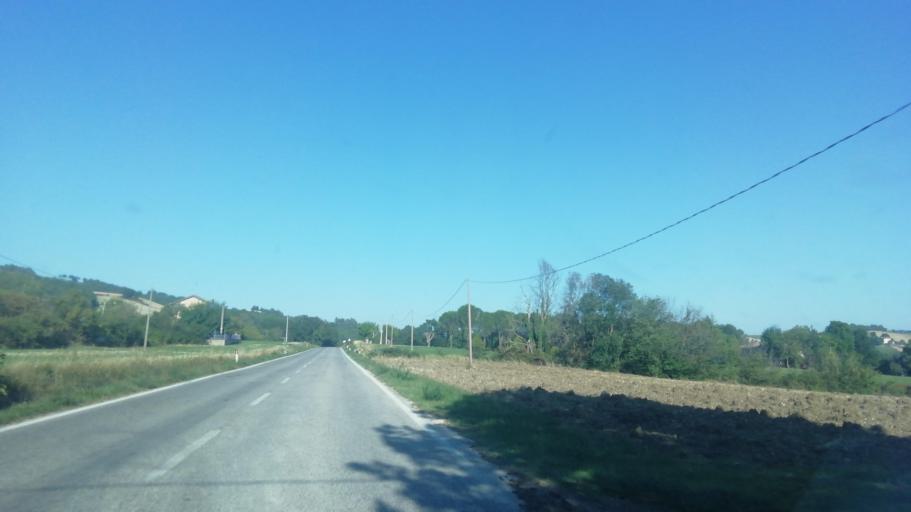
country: IT
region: The Marches
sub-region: Provincia di Pesaro e Urbino
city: Frontone
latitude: 43.5450
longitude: 12.7741
